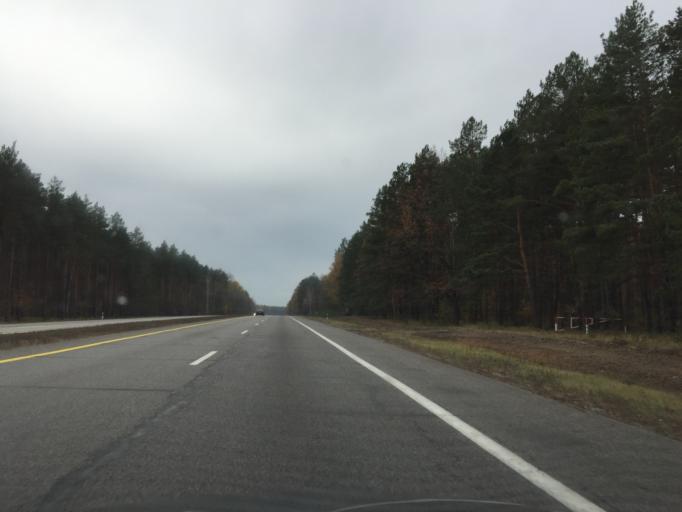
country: BY
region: Gomel
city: Gomel
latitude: 52.3666
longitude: 30.7441
